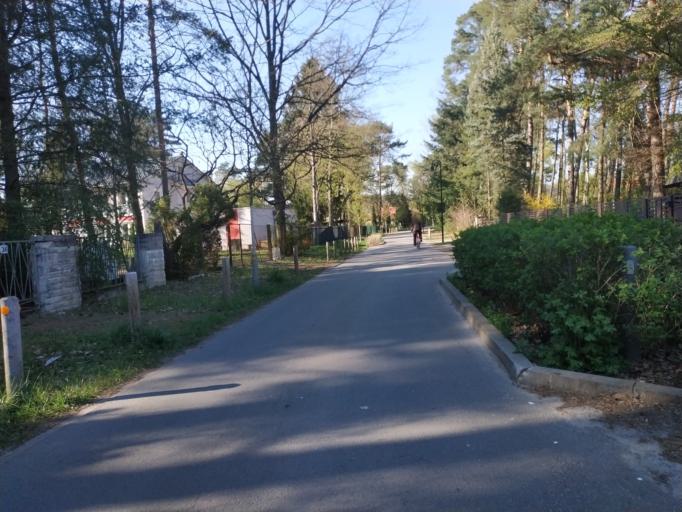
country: DE
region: Brandenburg
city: Petershagen
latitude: 52.5544
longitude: 13.8257
